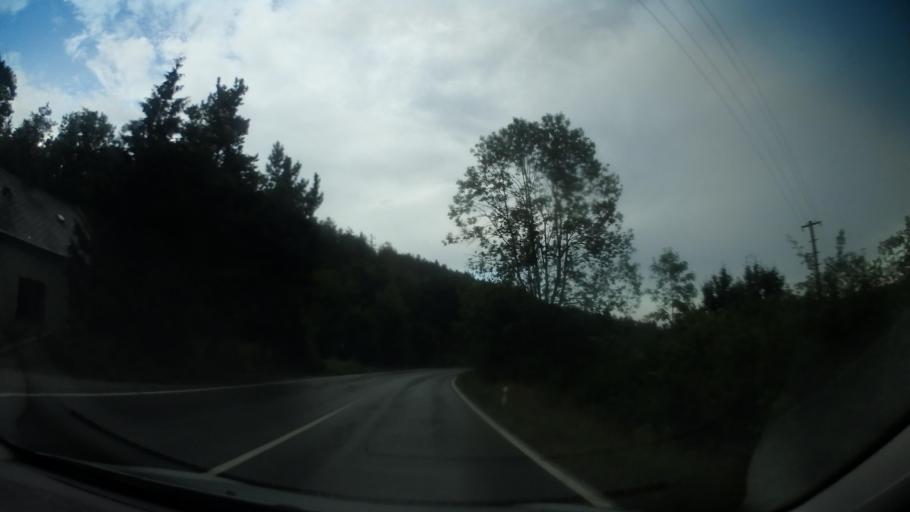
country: CZ
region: Olomoucky
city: Bila Lhota
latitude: 49.7033
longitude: 16.9913
